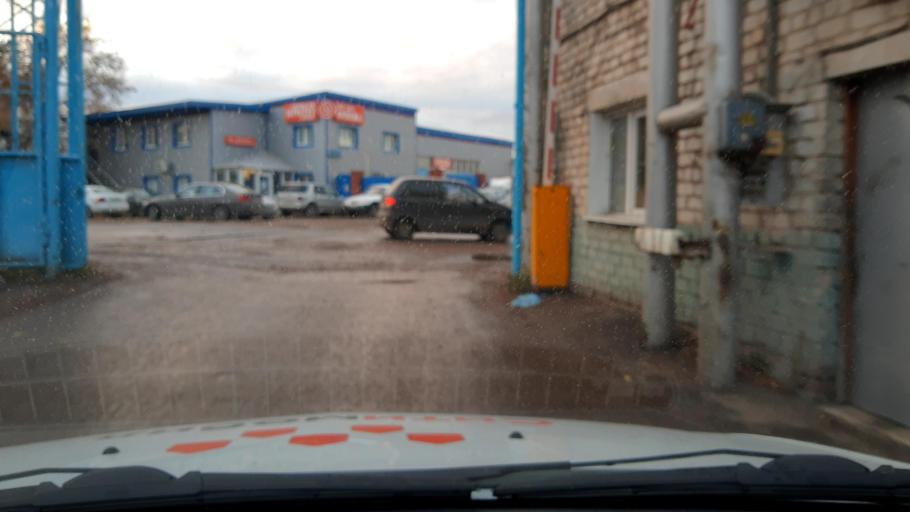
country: RU
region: Bashkortostan
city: Ufa
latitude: 54.7840
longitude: 56.0617
